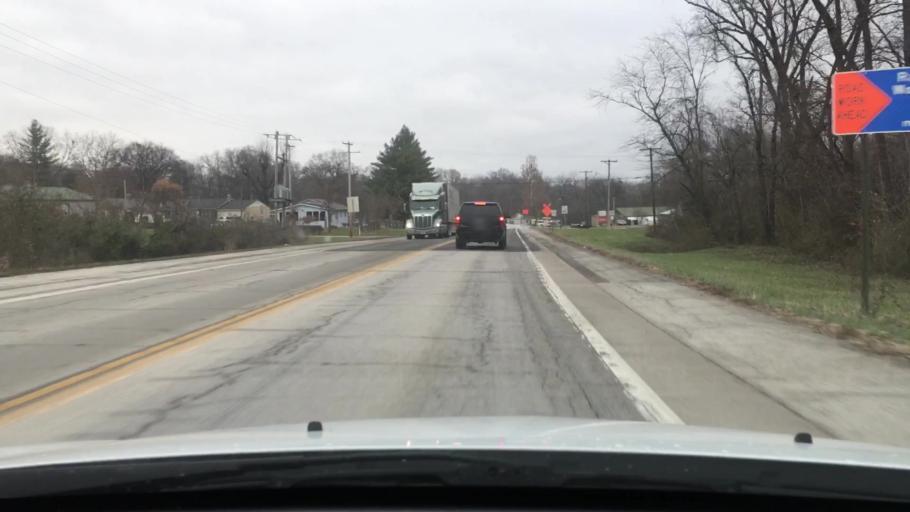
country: US
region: Missouri
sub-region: Pike County
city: Louisiana
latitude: 39.4519
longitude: -91.0612
